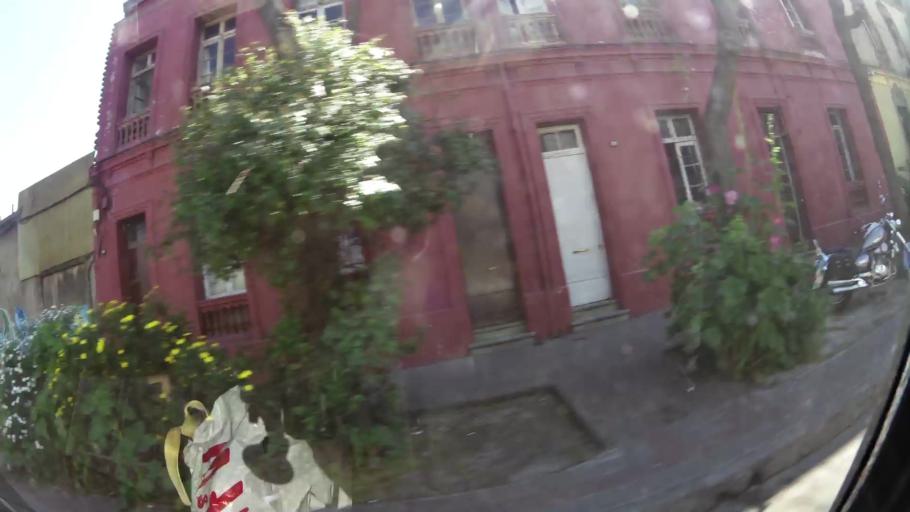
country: CL
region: Santiago Metropolitan
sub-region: Provincia de Santiago
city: Santiago
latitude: -33.4493
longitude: -70.6653
